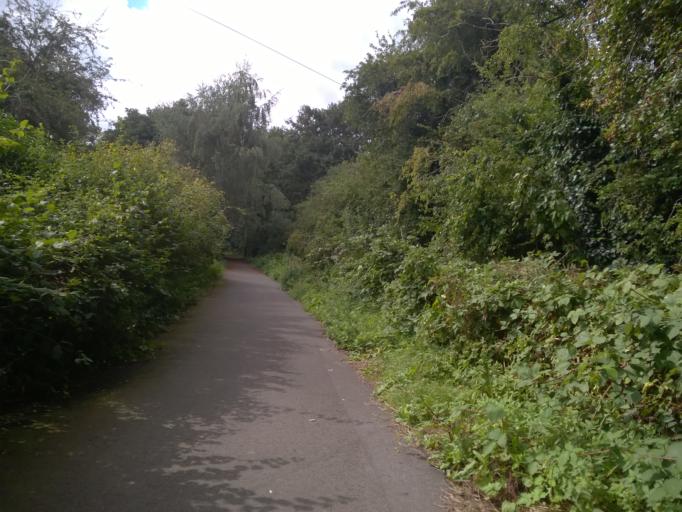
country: GB
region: England
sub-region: Leicestershire
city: Glenfield
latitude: 52.6536
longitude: -1.2008
